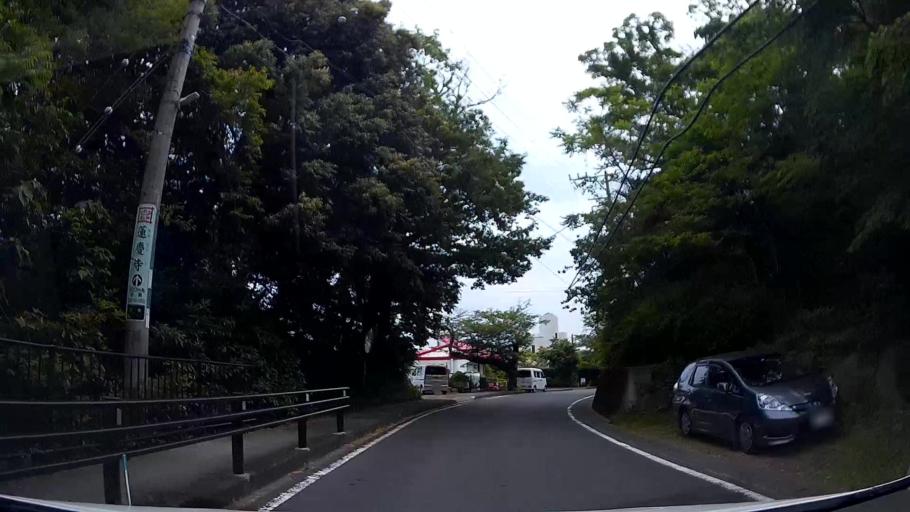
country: JP
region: Shizuoka
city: Ito
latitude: 34.9517
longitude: 139.1285
